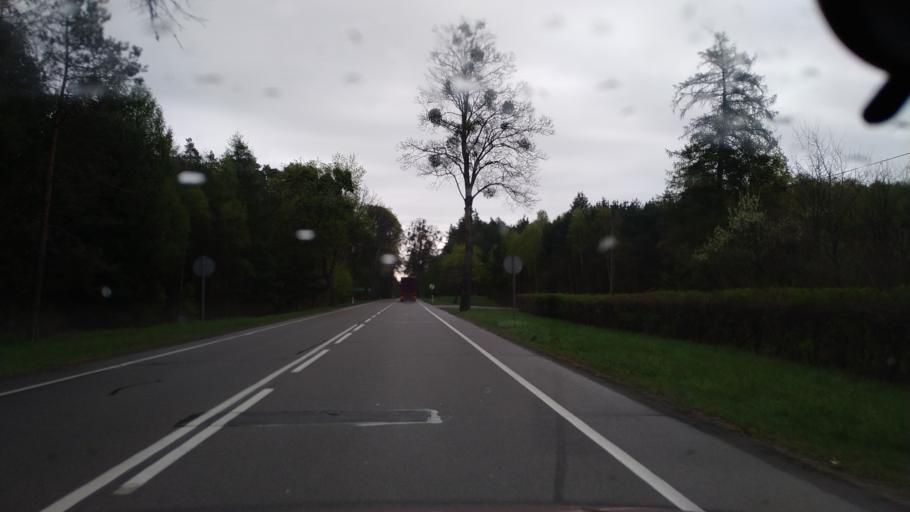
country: PL
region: Pomeranian Voivodeship
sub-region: Powiat starogardzki
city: Kaliska
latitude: 53.8781
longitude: 18.1825
